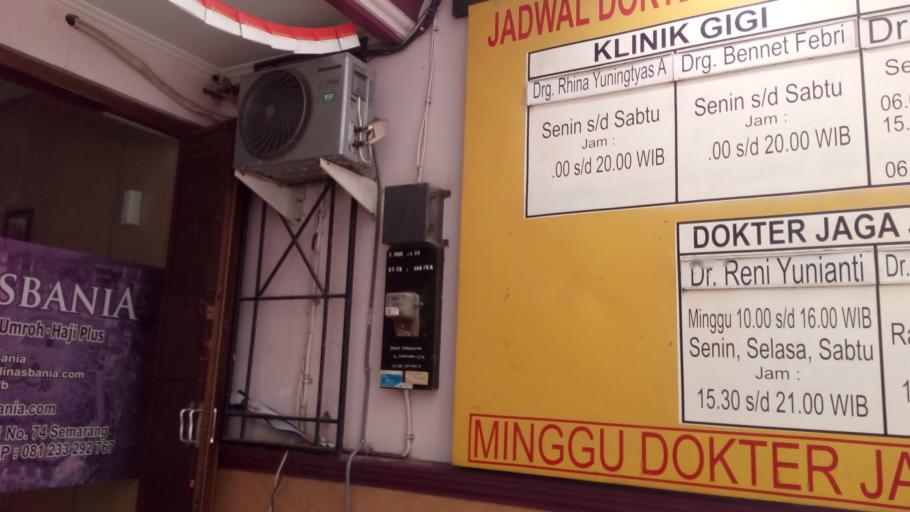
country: ID
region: Central Java
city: Semarang
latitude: -6.9789
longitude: 110.4608
